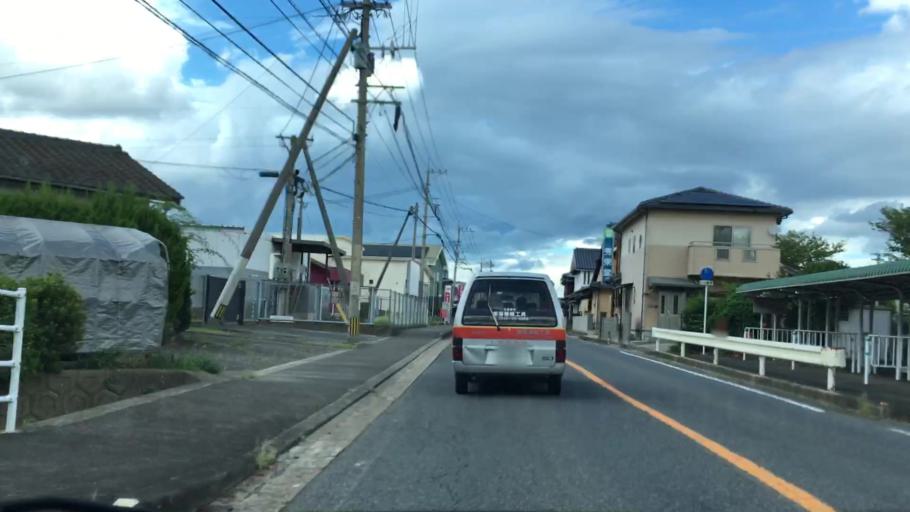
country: JP
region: Saga Prefecture
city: Imaricho-ko
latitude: 33.2015
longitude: 129.8503
